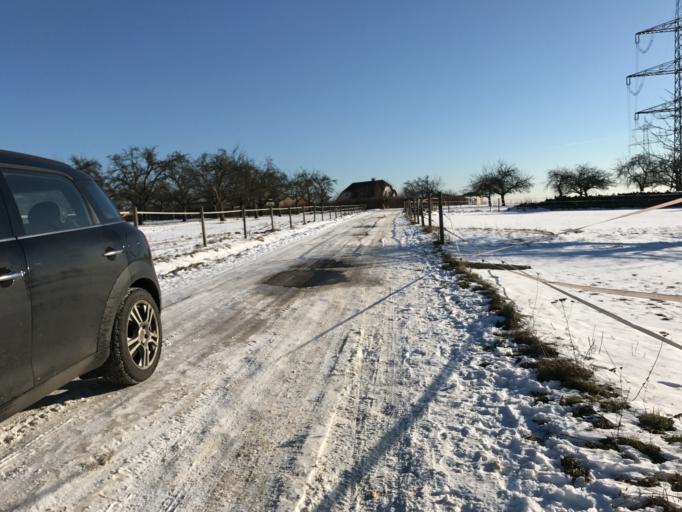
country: DE
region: Hesse
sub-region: Regierungsbezirk Darmstadt
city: Hofheim am Taunus
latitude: 50.0963
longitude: 8.4028
